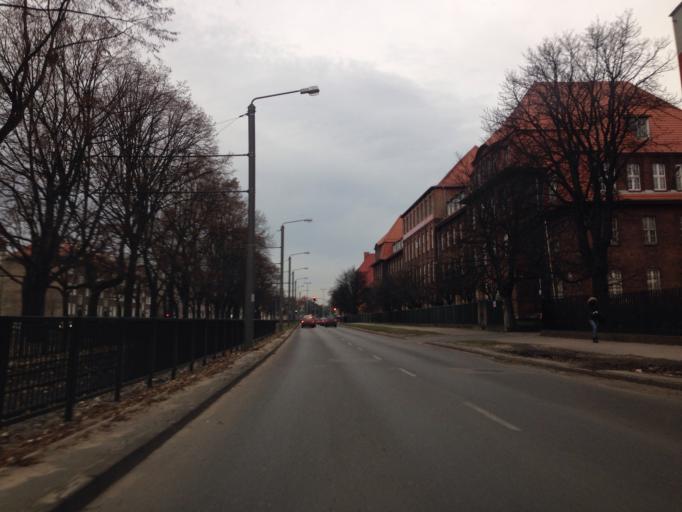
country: PL
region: Pomeranian Voivodeship
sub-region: Gdansk
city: Gdansk
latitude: 54.3842
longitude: 18.6141
